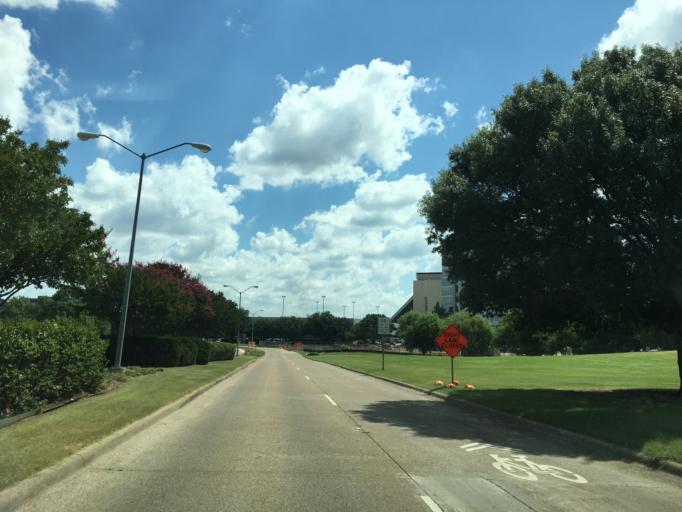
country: US
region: Texas
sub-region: Dallas County
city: Addison
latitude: 32.9258
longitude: -96.8465
